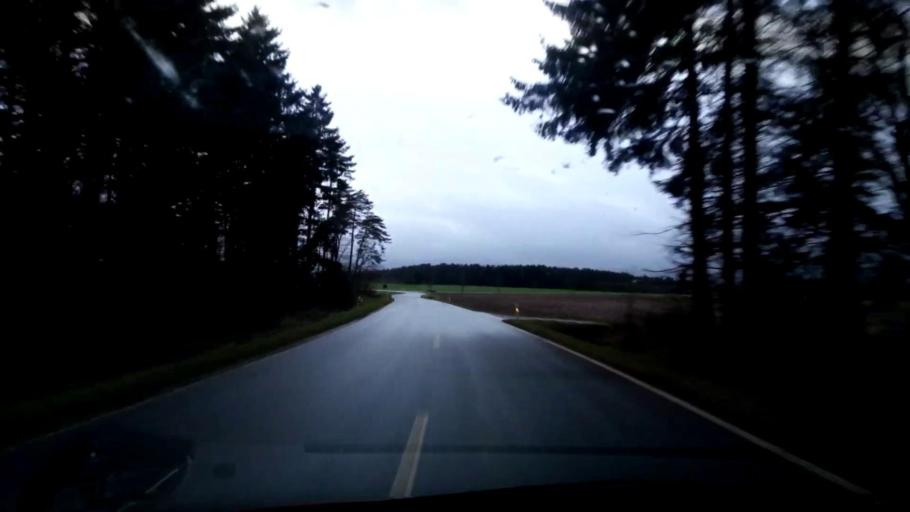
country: DE
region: Bavaria
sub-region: Upper Franconia
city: Aufsess
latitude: 49.9399
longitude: 11.2229
